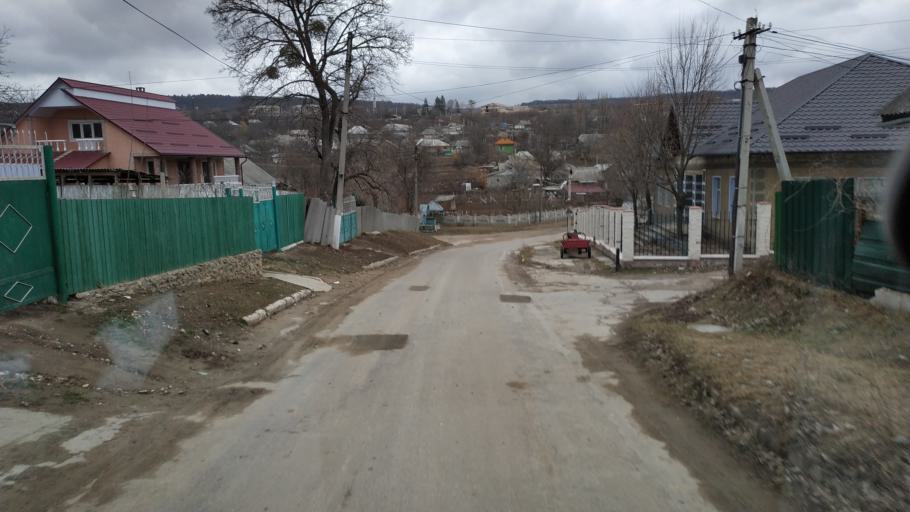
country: MD
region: Calarasi
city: Calarasi
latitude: 47.2043
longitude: 28.2484
